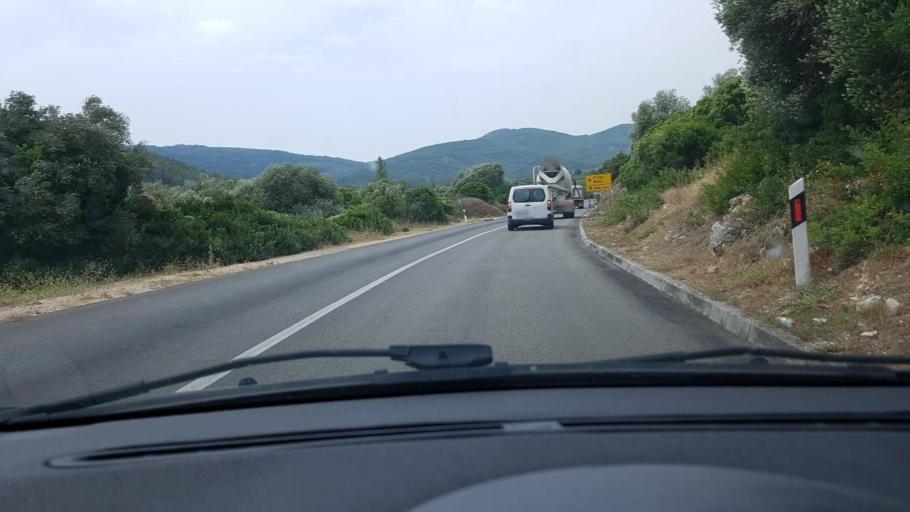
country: HR
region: Dubrovacko-Neretvanska
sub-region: Grad Dubrovnik
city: Vela Luka
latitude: 42.9477
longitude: 16.7789
